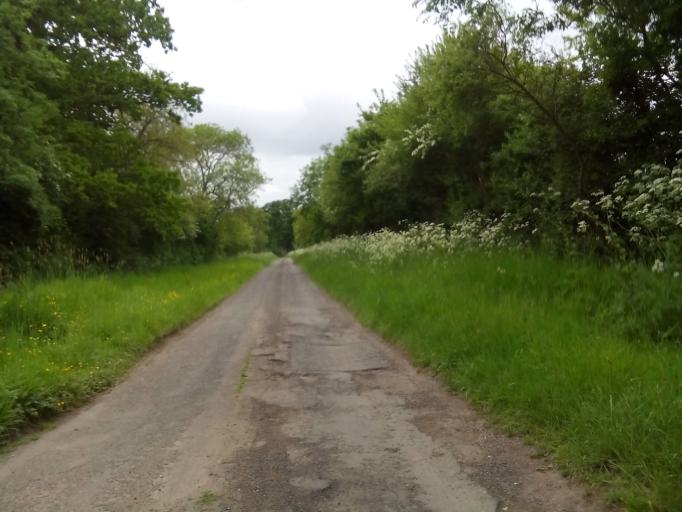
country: GB
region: England
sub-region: District of Rutland
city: Morcott
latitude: 52.5381
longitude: -0.5952
